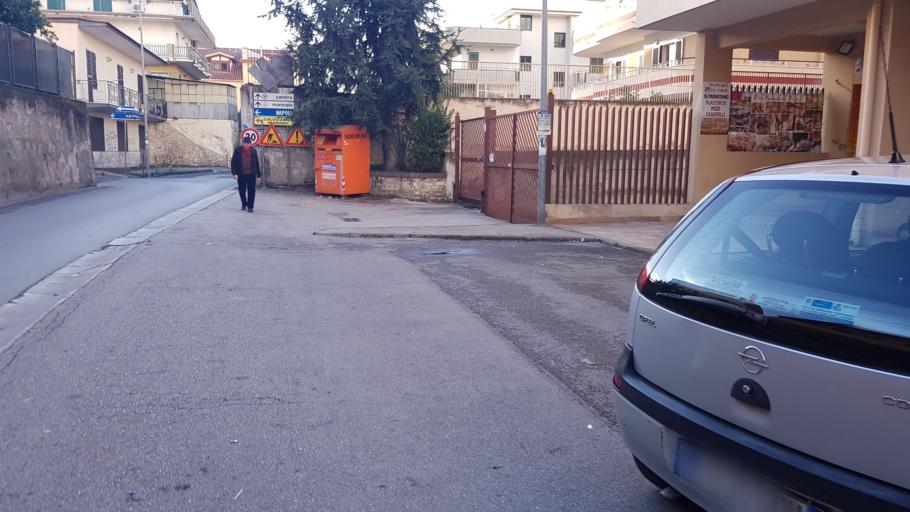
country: IT
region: Campania
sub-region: Provincia di Napoli
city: Mugnano di Napoli
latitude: 40.9081
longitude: 14.2105
